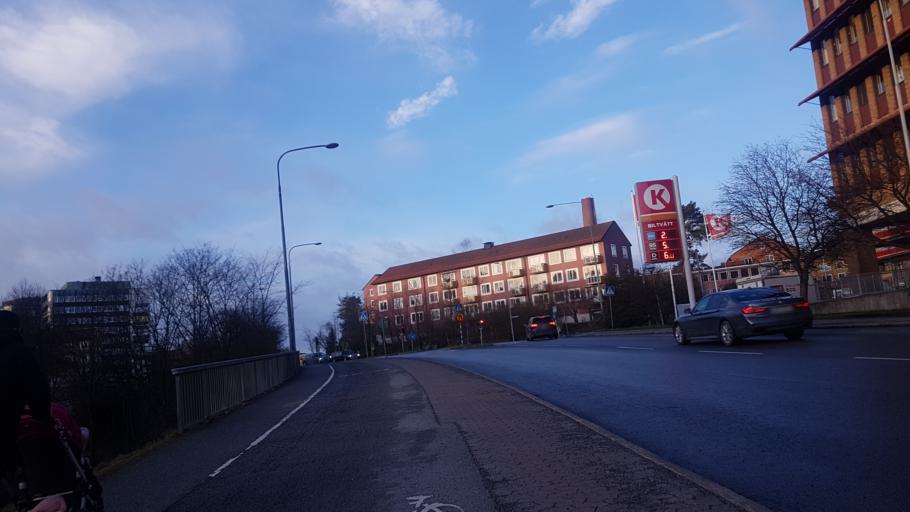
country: SE
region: Stockholm
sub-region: Lidingo
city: Lidingoe
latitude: 59.3647
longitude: 18.1267
